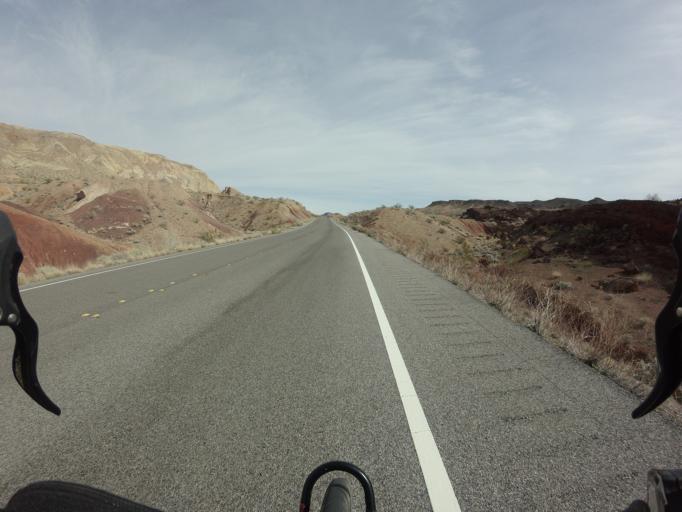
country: US
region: Nevada
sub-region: Clark County
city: Boulder City
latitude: 36.1940
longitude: -114.7159
